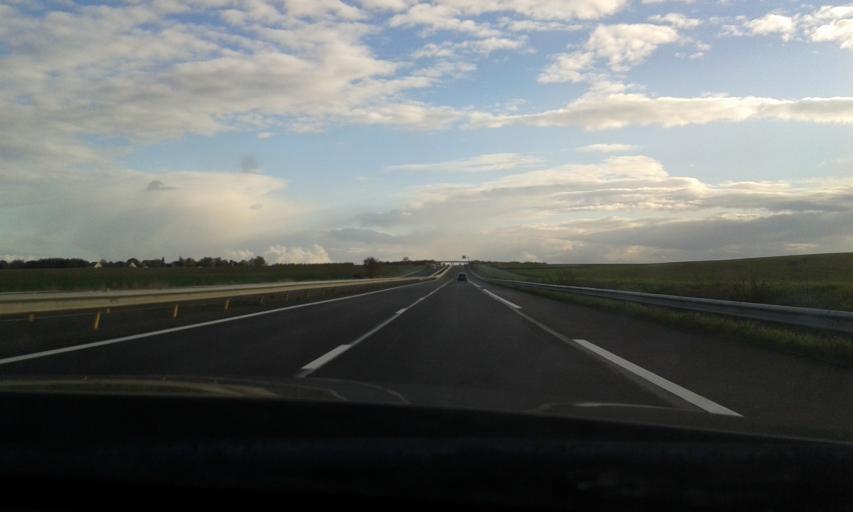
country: FR
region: Centre
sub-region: Departement d'Eure-et-Loir
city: Leves
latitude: 48.5165
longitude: 1.4595
